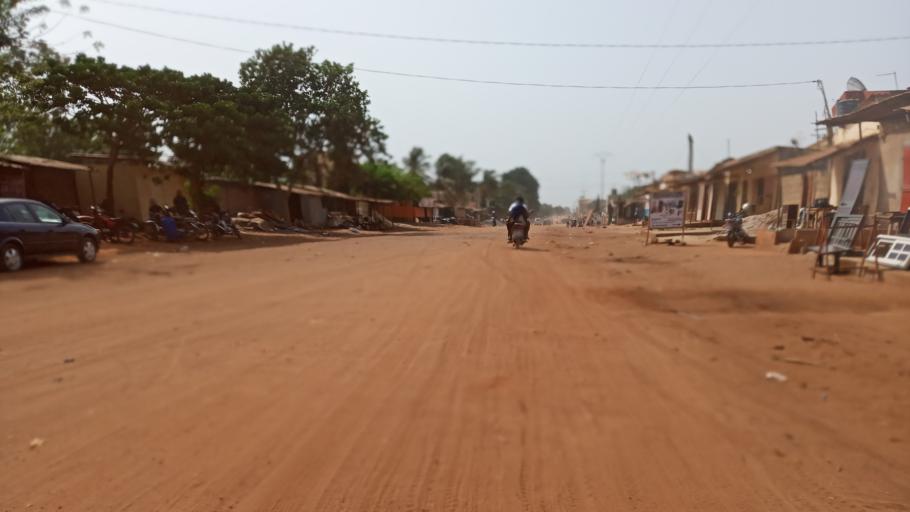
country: TG
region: Maritime
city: Lome
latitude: 6.2061
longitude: 1.1633
